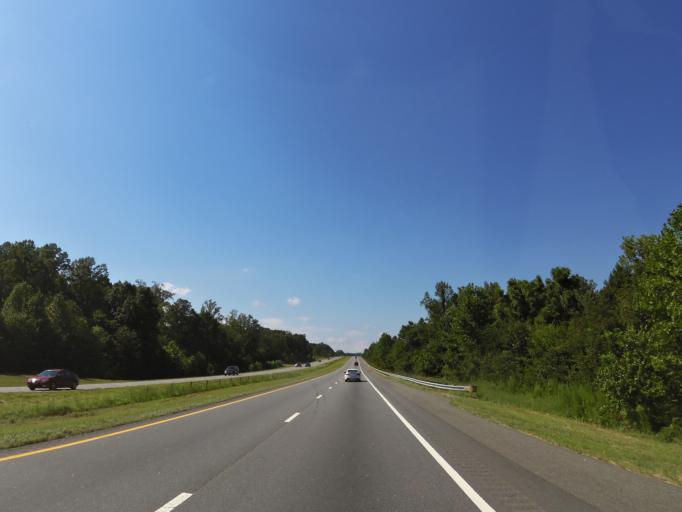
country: US
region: North Carolina
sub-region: Catawba County
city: Mountain View
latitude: 35.6660
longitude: -81.3283
